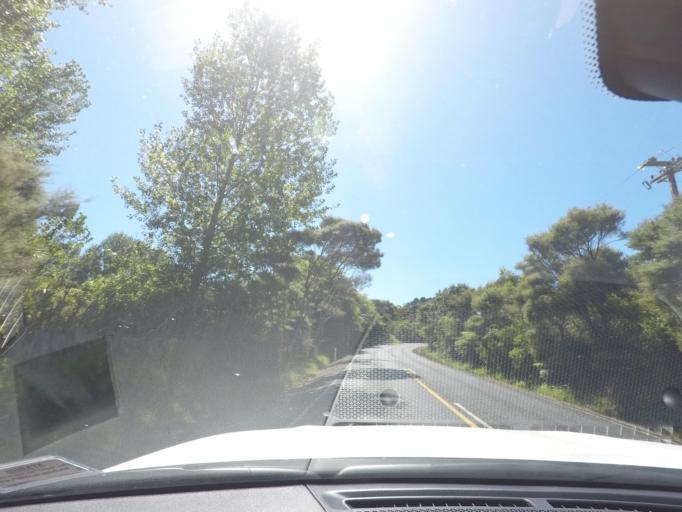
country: NZ
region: Auckland
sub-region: Auckland
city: Parakai
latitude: -36.6136
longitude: 174.3402
